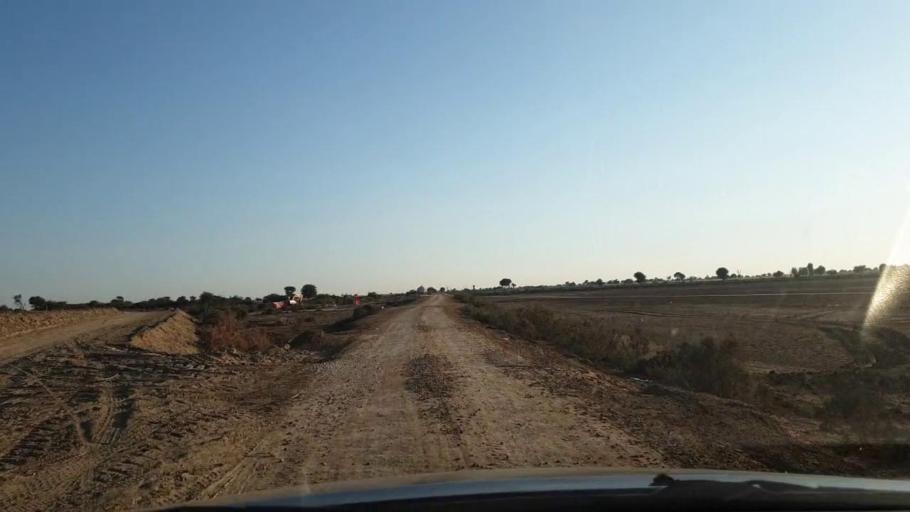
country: PK
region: Sindh
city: Tando Mittha Khan
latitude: 25.8348
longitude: 69.1740
